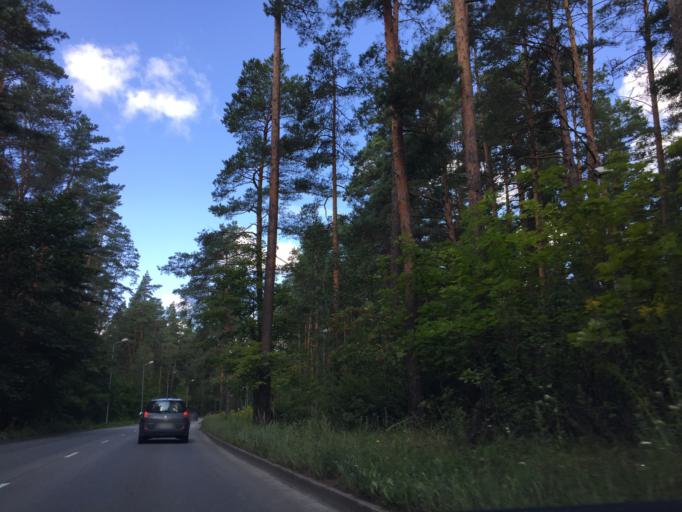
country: LV
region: Stopini
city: Ulbroka
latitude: 56.9754
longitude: 24.2229
